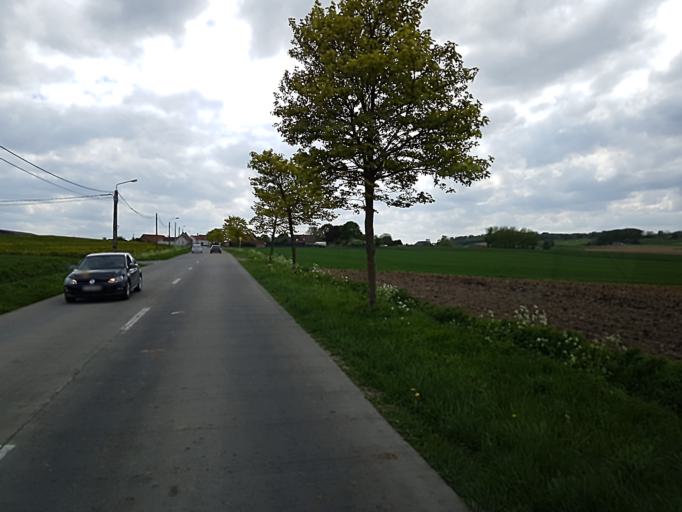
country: BE
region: Wallonia
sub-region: Province du Hainaut
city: Celles
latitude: 50.6625
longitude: 3.4395
